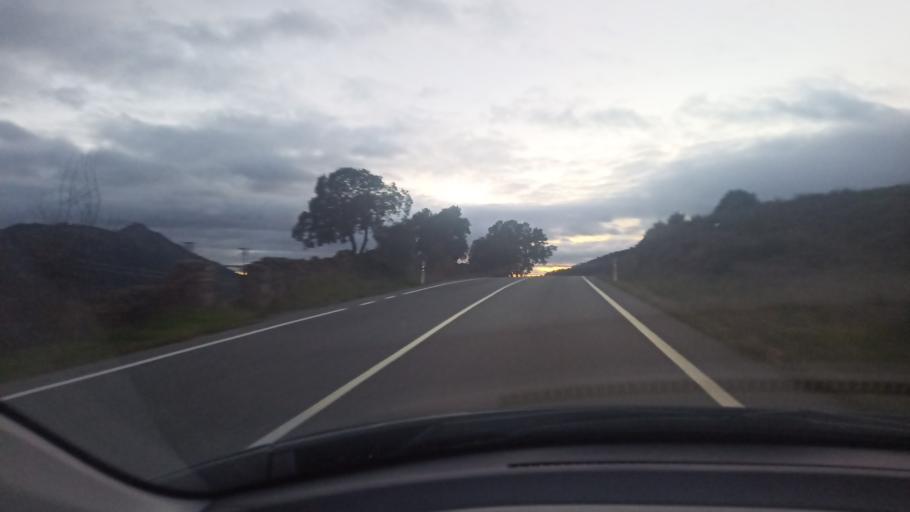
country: ES
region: Madrid
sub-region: Provincia de Madrid
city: Robledo de Chavela
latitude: 40.4876
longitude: -4.2483
